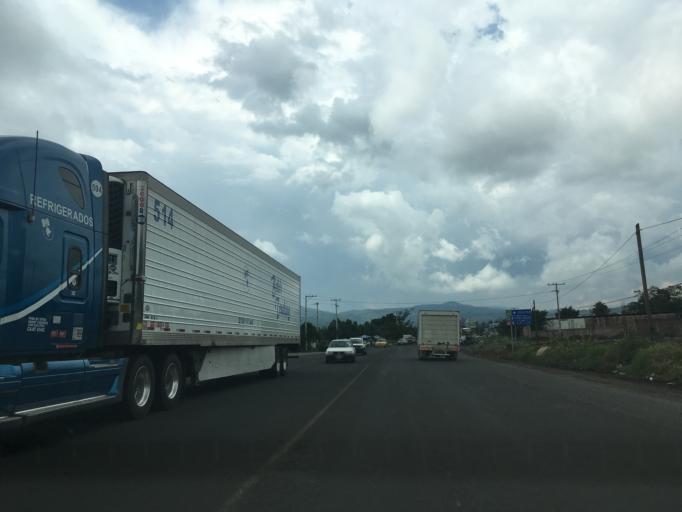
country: MX
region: Michoacan
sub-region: Los Reyes
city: La Higuerita (Colonia San Rafael)
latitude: 19.6207
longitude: -102.4865
